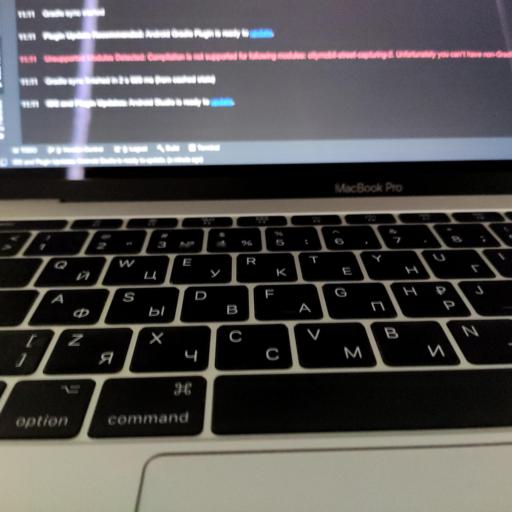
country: RU
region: Krasnodarskiy
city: Adler
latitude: 43.4369
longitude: 39.9252
